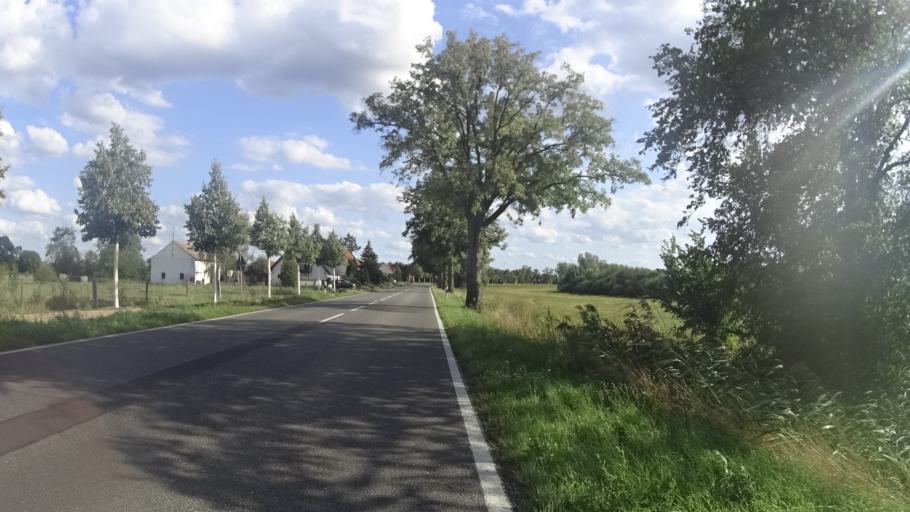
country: DE
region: Brandenburg
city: Rathenow
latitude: 52.6339
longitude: 12.3310
